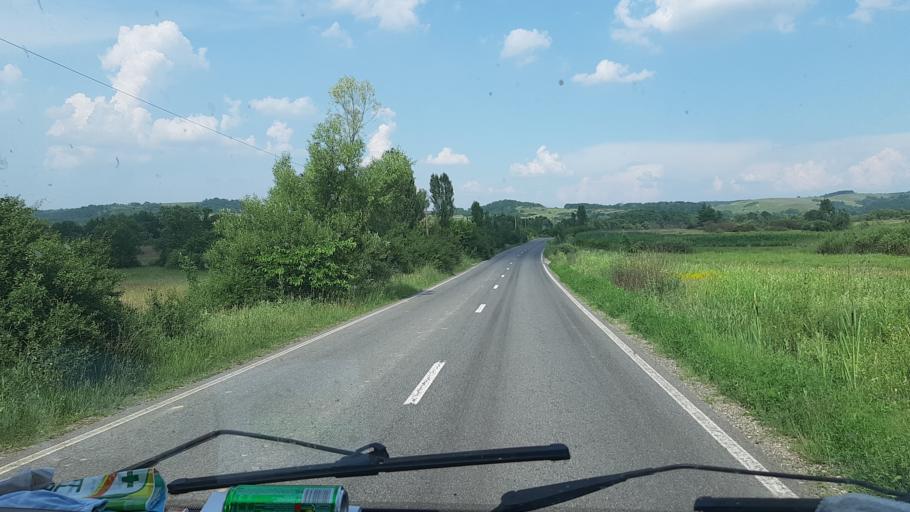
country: RO
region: Caras-Severin
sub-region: Comuna Farliug
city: Farliug
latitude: 45.5022
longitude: 21.8635
